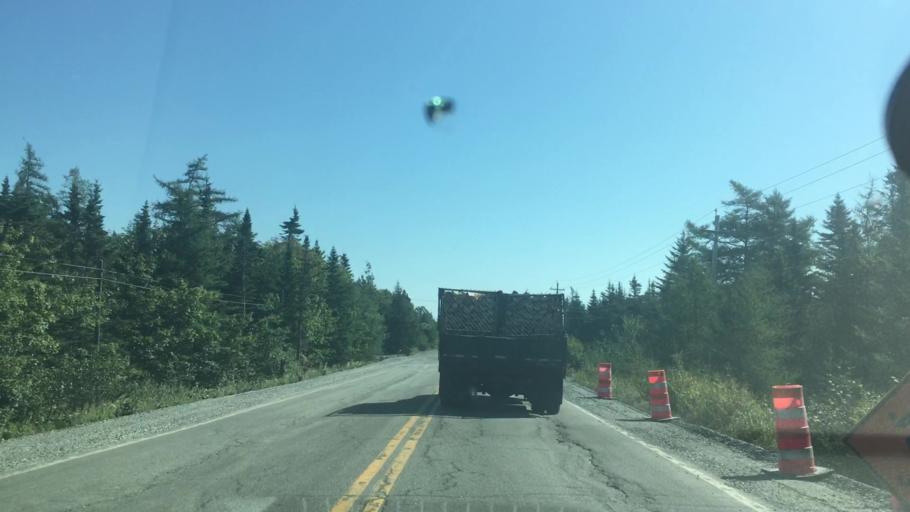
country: CA
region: Nova Scotia
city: New Glasgow
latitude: 44.9041
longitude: -62.4638
